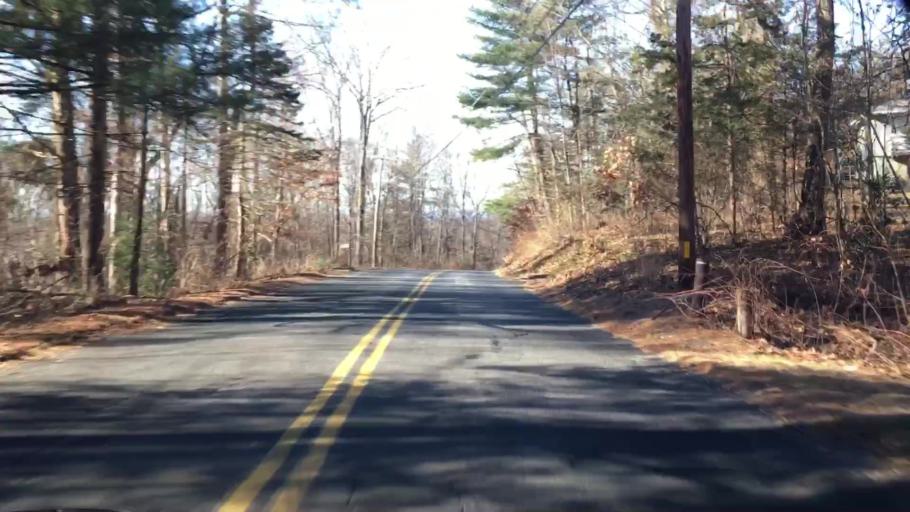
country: US
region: Connecticut
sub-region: Tolland County
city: Somers
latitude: 41.9702
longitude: -72.4387
